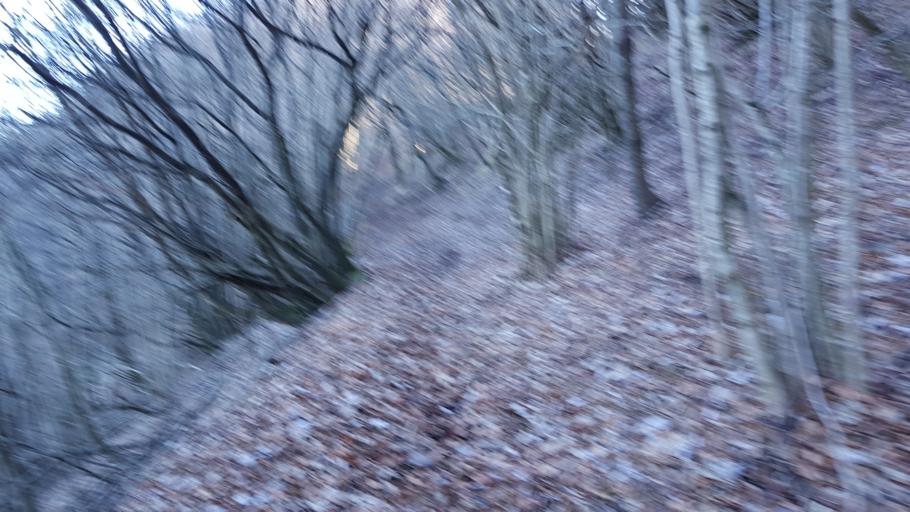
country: IT
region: Liguria
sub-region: Provincia di Genova
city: Torriglia
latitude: 44.5422
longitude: 9.1553
